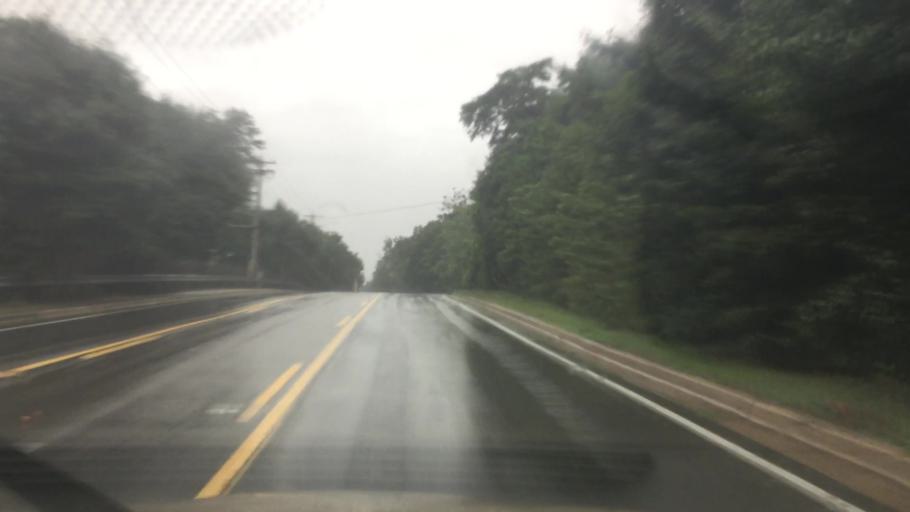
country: US
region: Maryland
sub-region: Anne Arundel County
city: Severn
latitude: 39.1358
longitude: -76.7154
